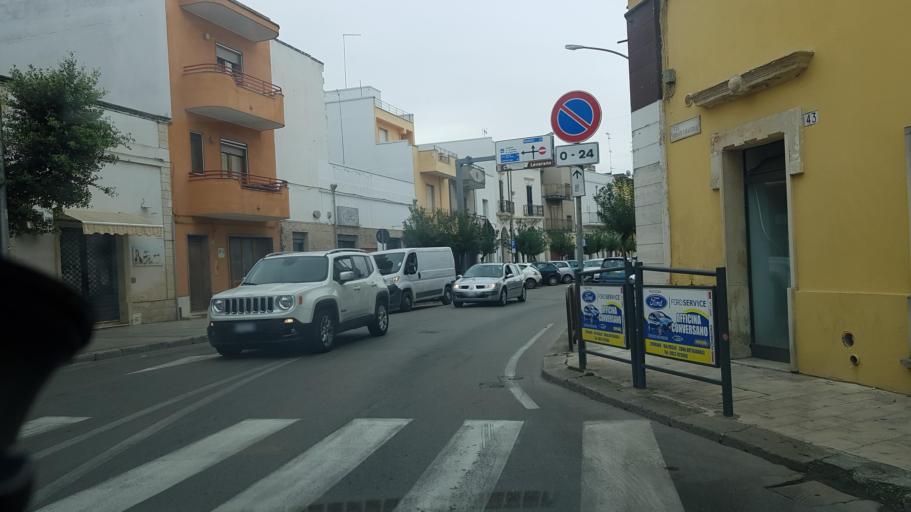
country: IT
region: Apulia
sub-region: Provincia di Lecce
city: Leverano
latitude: 40.2906
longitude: 17.9998
